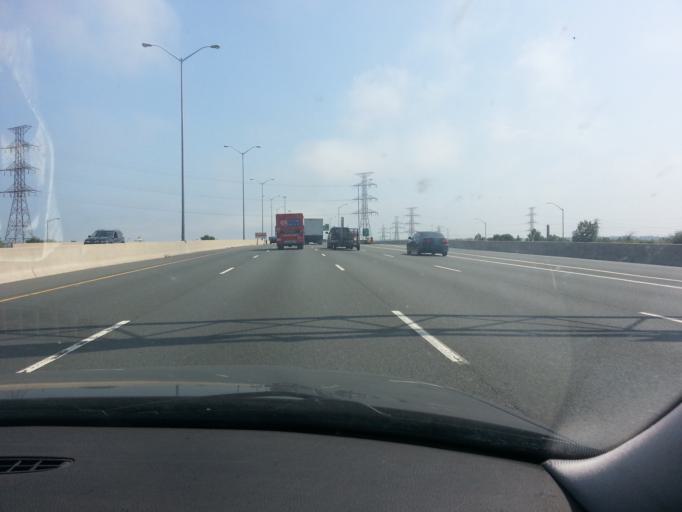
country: CA
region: Ontario
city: Hamilton
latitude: 43.2659
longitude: -79.7747
